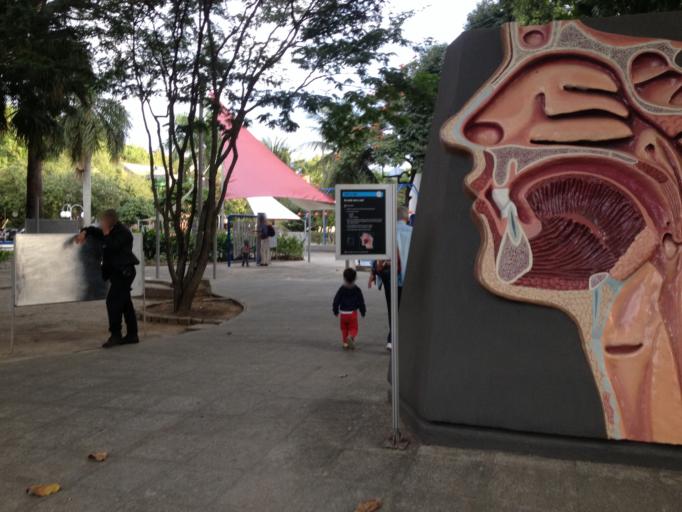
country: BR
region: Rio de Janeiro
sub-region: Rio De Janeiro
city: Rio de Janeiro
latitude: -22.8771
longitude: -43.2443
